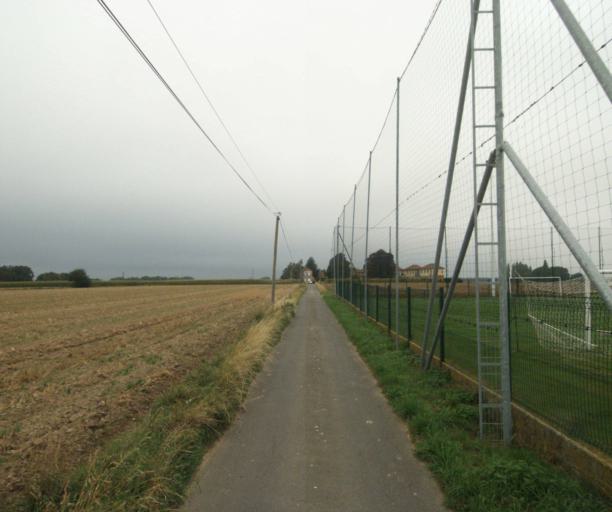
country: FR
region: Nord-Pas-de-Calais
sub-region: Departement du Nord
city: Sailly-lez-Lannoy
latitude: 50.6448
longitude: 3.2152
